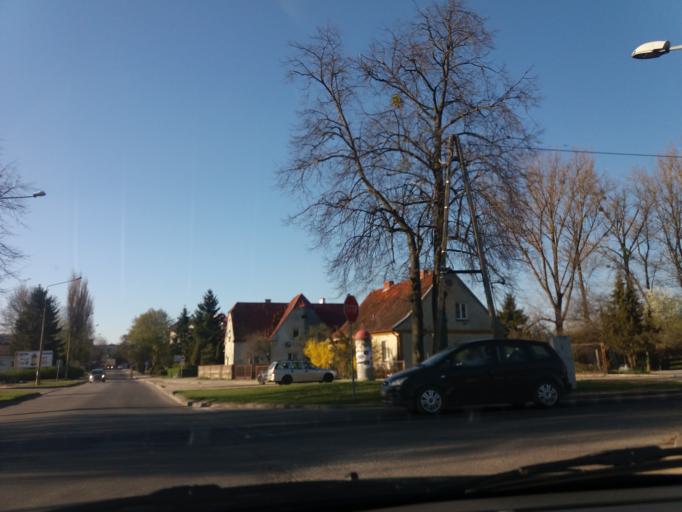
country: PL
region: Warmian-Masurian Voivodeship
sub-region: Powiat nidzicki
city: Nidzica
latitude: 53.3532
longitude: 20.4278
